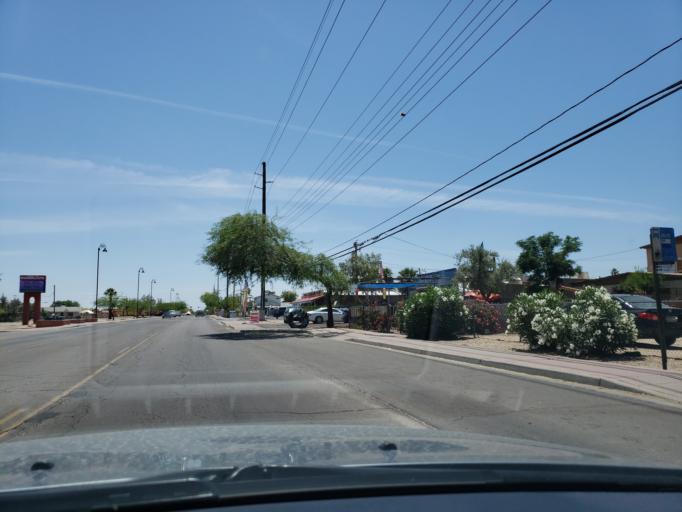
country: US
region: Arizona
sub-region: Maricopa County
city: Guadalupe
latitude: 33.3676
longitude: -111.9632
